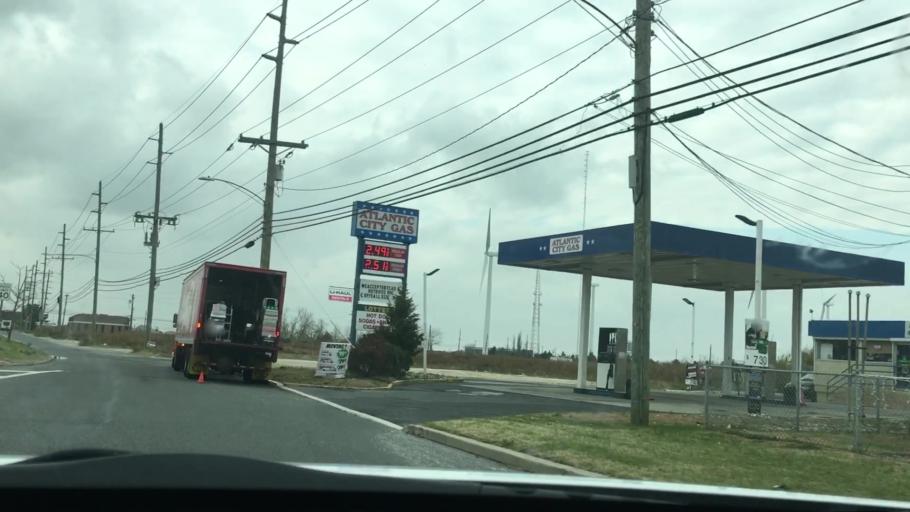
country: US
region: New Jersey
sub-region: Atlantic County
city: Atlantic City
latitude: 39.3752
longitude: -74.4446
